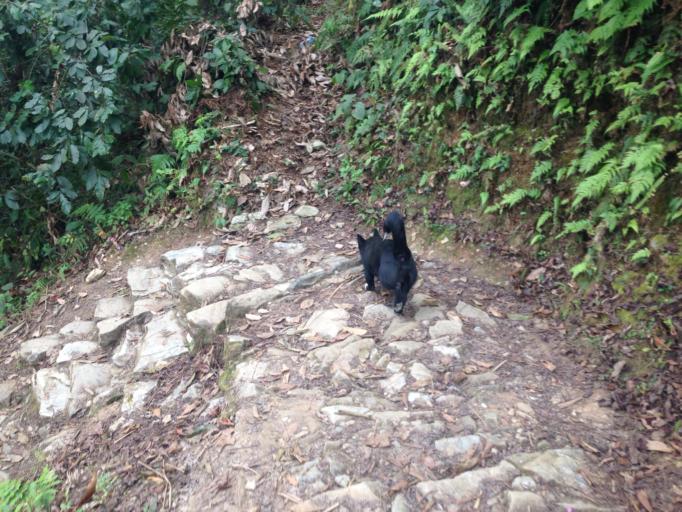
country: NP
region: Western Region
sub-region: Gandaki Zone
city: Pokhara
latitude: 28.2054
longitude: 83.9460
